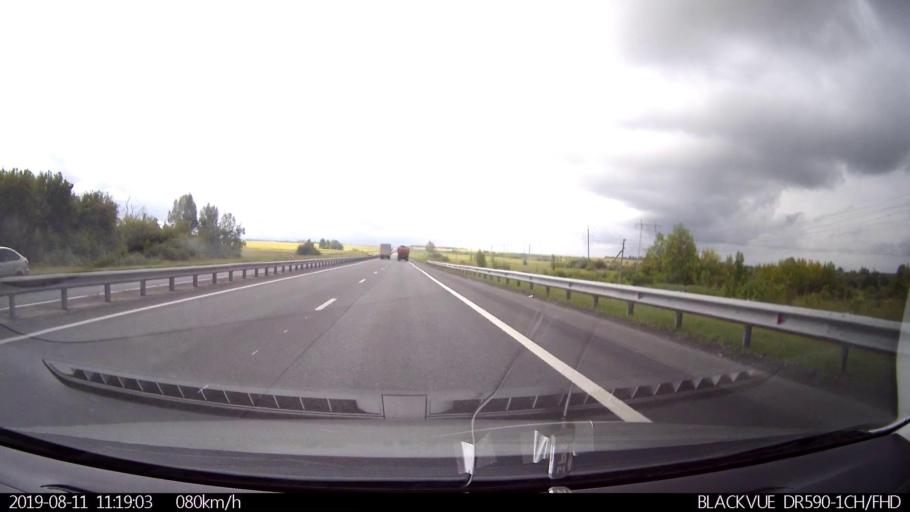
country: RU
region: Ulyanovsk
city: Novoul'yanovsk
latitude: 54.1728
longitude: 48.2650
